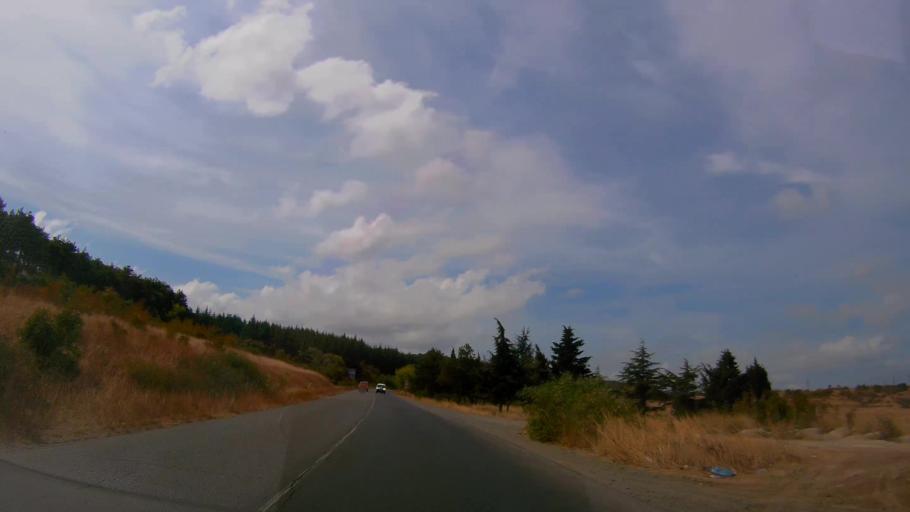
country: BG
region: Burgas
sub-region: Obshtina Sozopol
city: Sozopol
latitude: 42.4086
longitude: 27.6932
